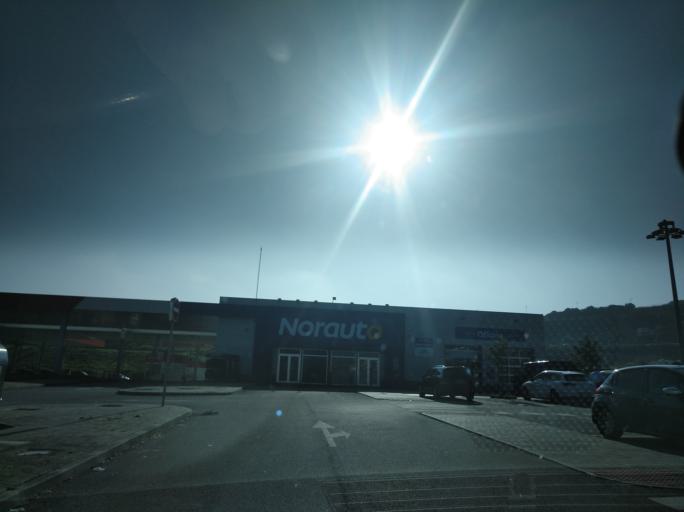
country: PT
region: Lisbon
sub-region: Odivelas
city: Famoes
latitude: 38.7741
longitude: -9.2161
